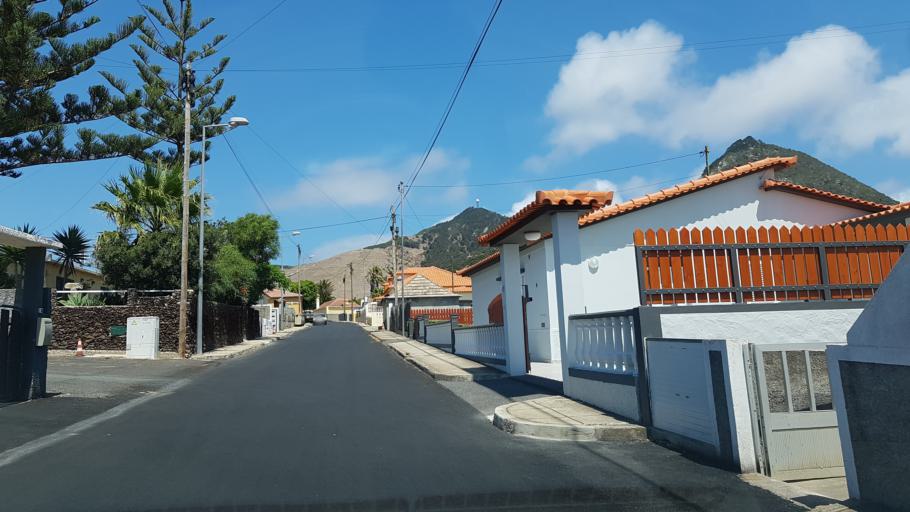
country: PT
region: Madeira
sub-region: Porto Santo
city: Camacha
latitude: 33.0858
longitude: -16.3467
